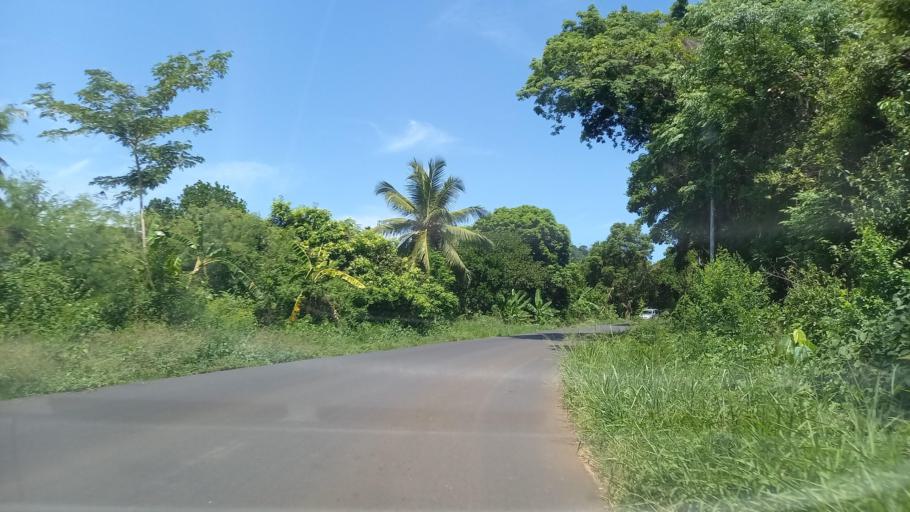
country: YT
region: M'Tsangamouji
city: M'Tsangamouji
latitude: -12.7494
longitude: 45.0604
